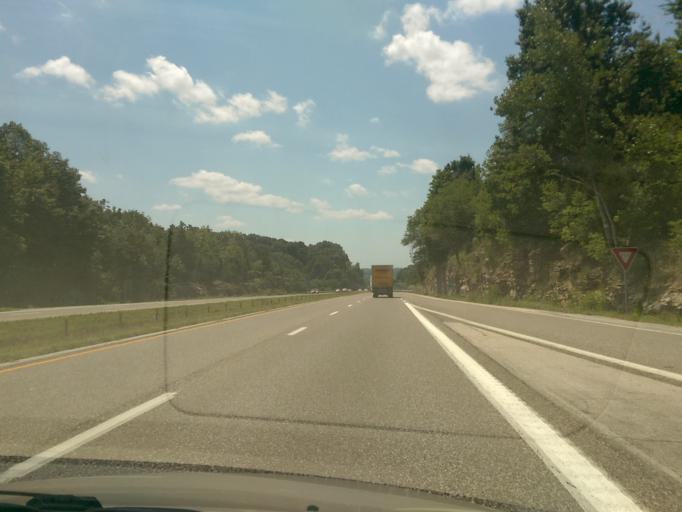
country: US
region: Missouri
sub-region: Boone County
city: Columbia
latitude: 38.9657
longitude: -92.5360
